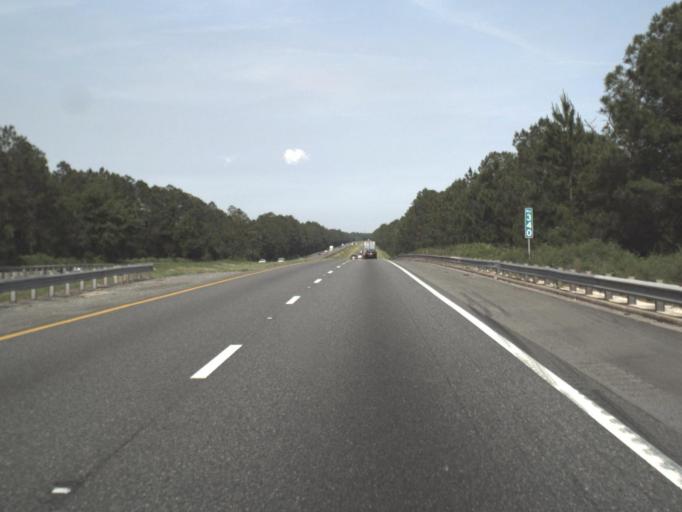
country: US
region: Florida
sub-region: Baker County
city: Macclenny
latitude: 30.2814
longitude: -82.0491
